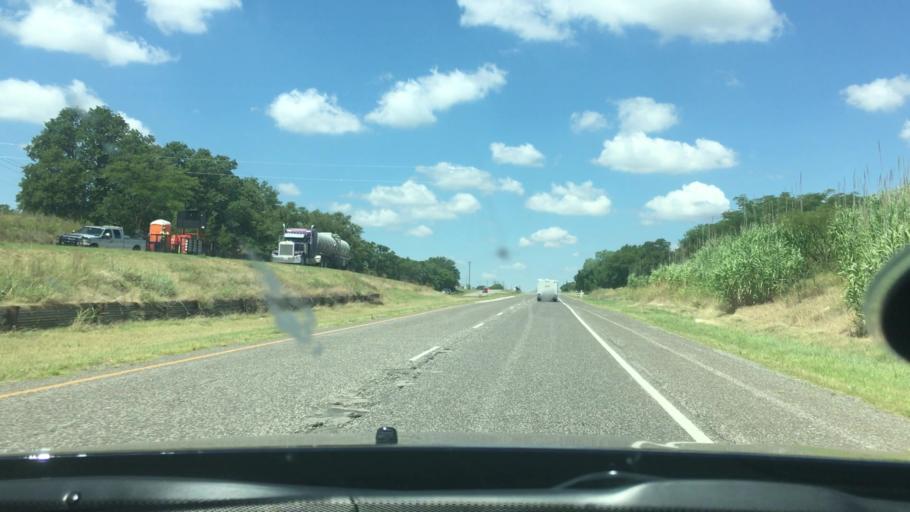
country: US
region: Oklahoma
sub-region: Carter County
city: Lone Grove
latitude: 34.1730
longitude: -97.3224
